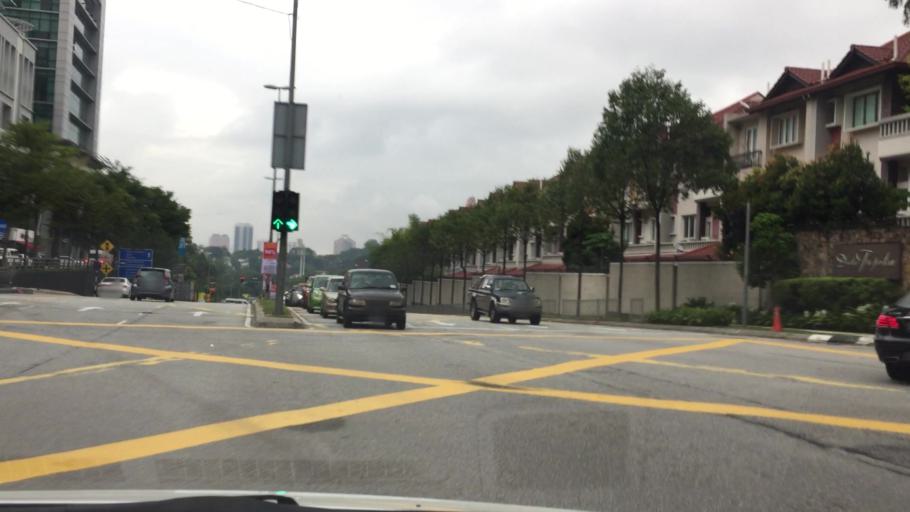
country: MY
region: Kuala Lumpur
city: Kuala Lumpur
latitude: 3.1703
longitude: 101.6660
